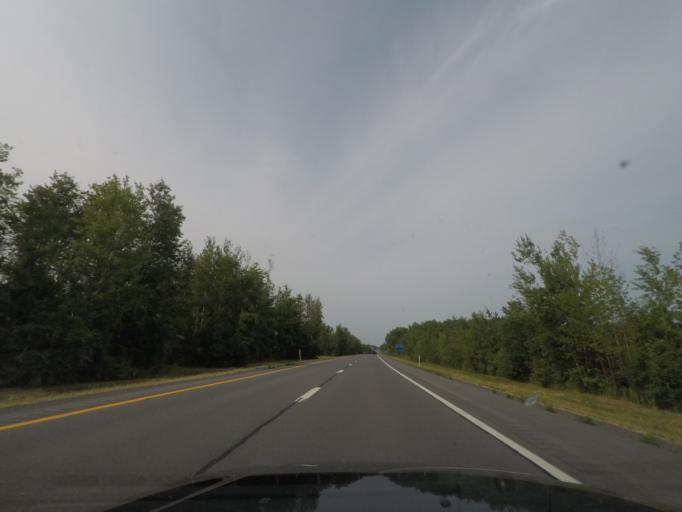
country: US
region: New York
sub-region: Clinton County
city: Peru
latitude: 44.5644
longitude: -73.5036
